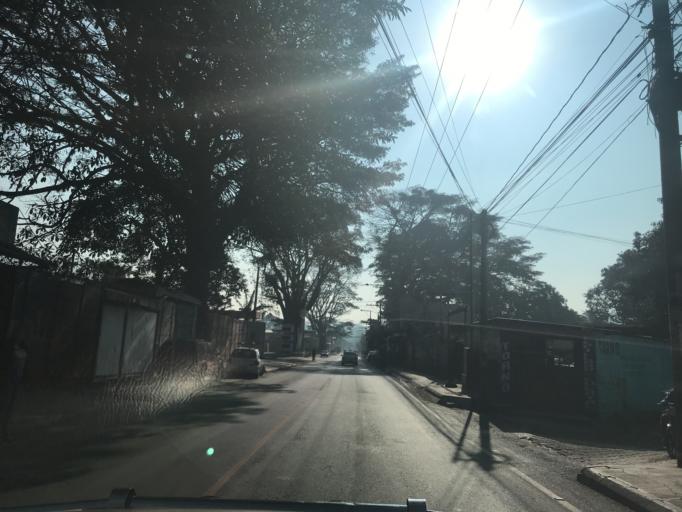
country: GT
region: Guatemala
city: Amatitlan
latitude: 14.4882
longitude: -90.6229
